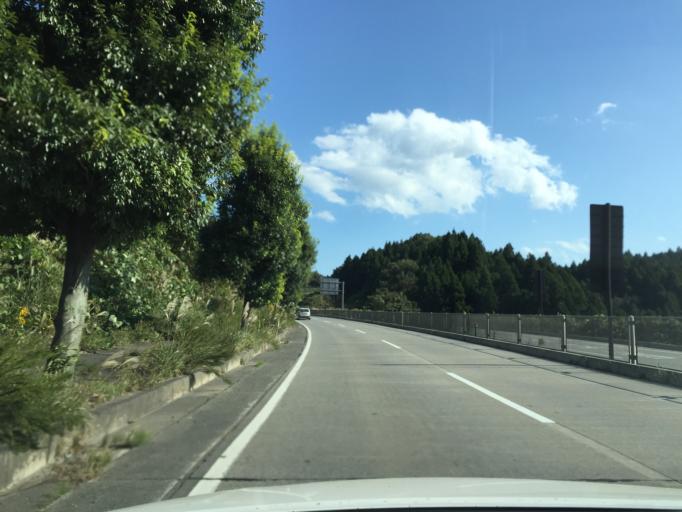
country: JP
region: Fukushima
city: Iwaki
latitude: 37.0240
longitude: 140.8848
